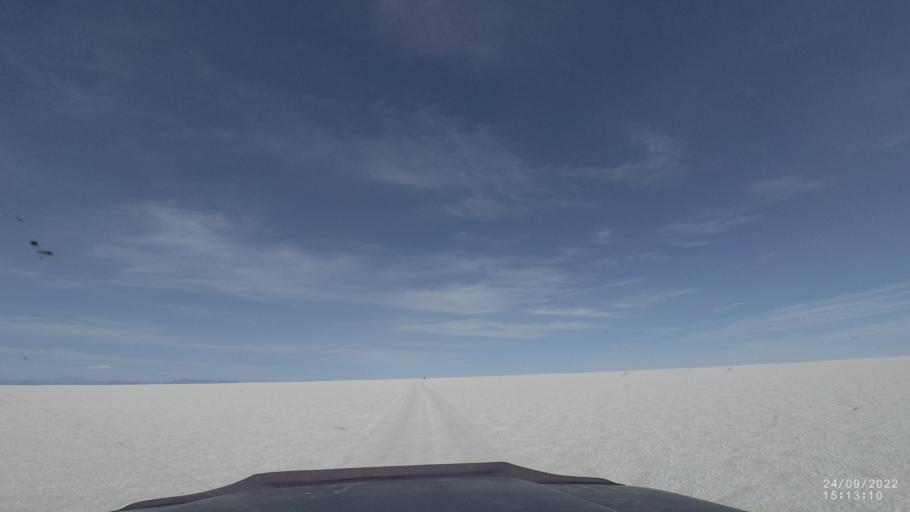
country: BO
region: Potosi
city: Colchani
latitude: -19.9536
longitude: -67.4678
